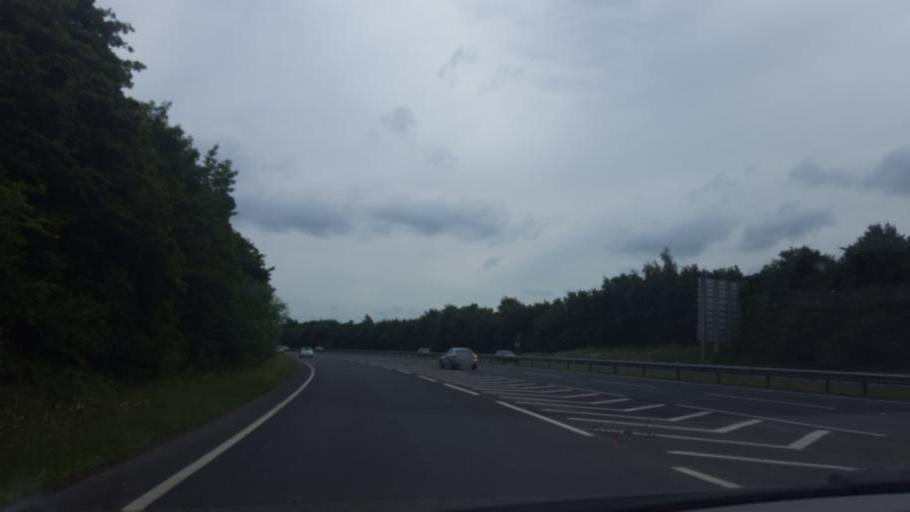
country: GB
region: England
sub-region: Royal Borough of Windsor and Maidenhead
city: Bisham
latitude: 51.5279
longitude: -0.7828
